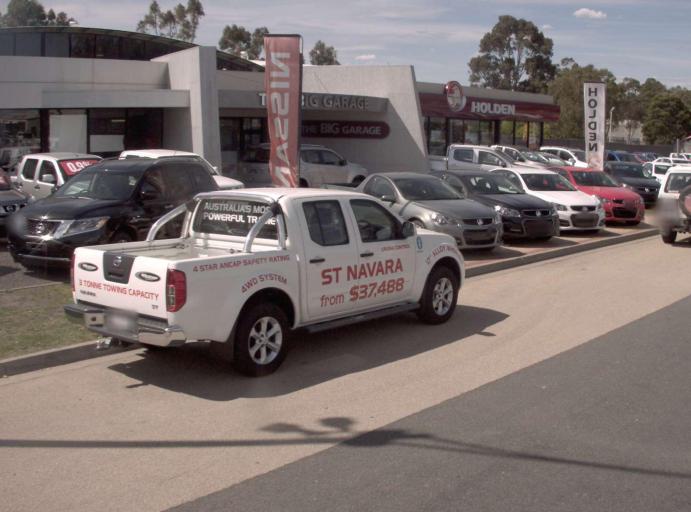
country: AU
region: Victoria
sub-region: East Gippsland
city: Bairnsdale
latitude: -37.8386
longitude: 147.5953
